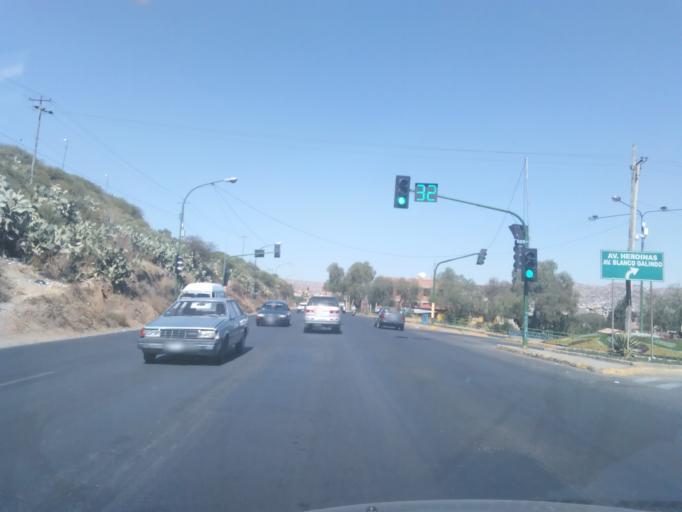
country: BO
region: Cochabamba
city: Cochabamba
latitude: -17.3888
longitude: -66.1406
